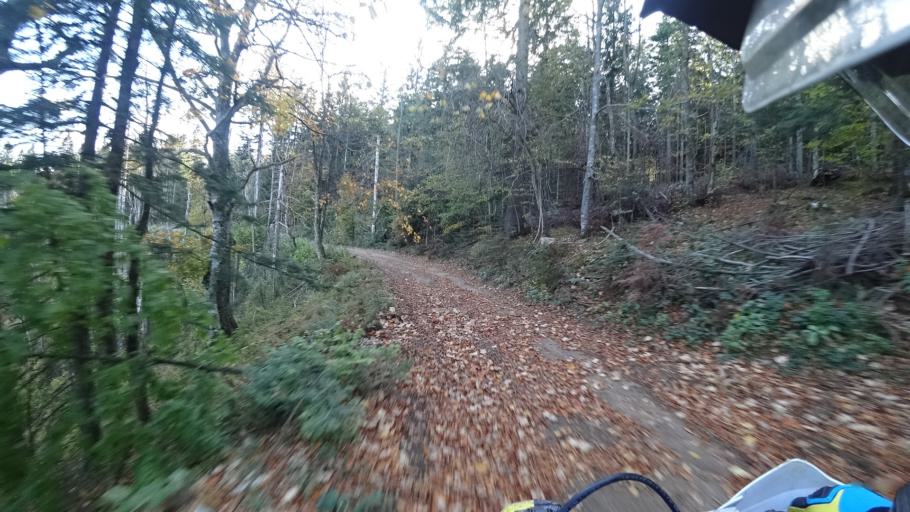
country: HR
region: Karlovacka
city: Plaski
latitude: 44.9553
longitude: 15.4478
